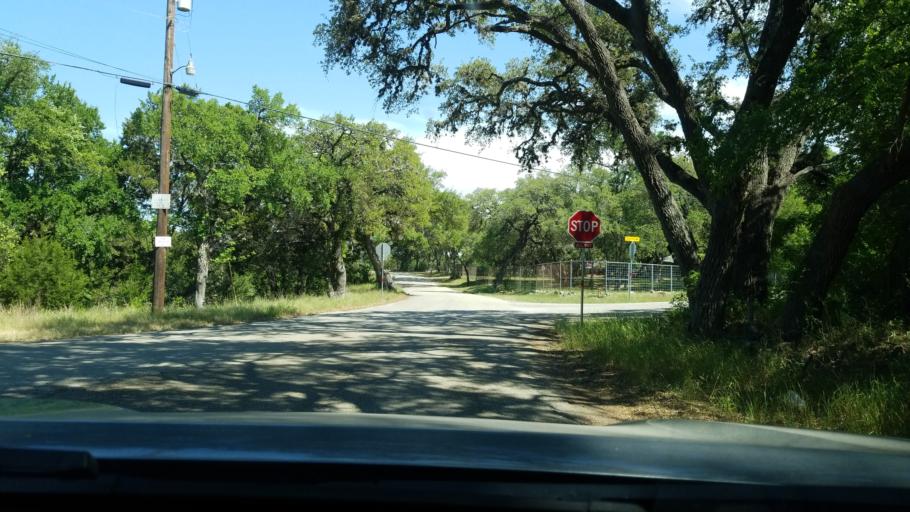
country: US
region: Texas
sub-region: Bexar County
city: Timberwood Park
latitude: 29.7489
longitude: -98.5155
